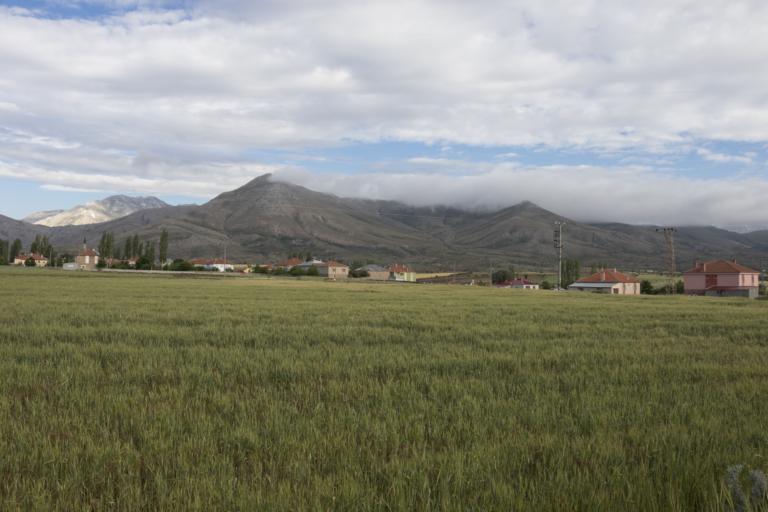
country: TR
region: Kayseri
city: Toklar
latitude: 38.4093
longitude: 36.0759
